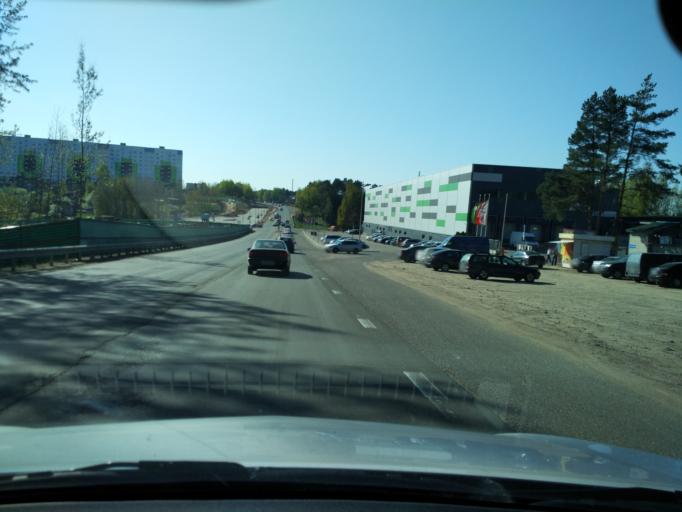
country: BY
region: Minsk
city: Borovlyany
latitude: 53.9637
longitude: 27.6752
